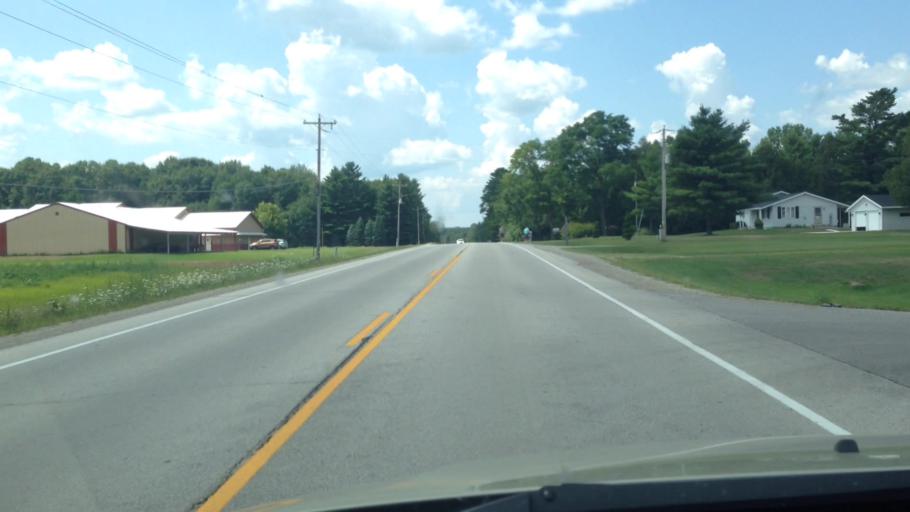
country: US
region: Wisconsin
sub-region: Brown County
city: Suamico
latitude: 44.6426
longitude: -88.0843
